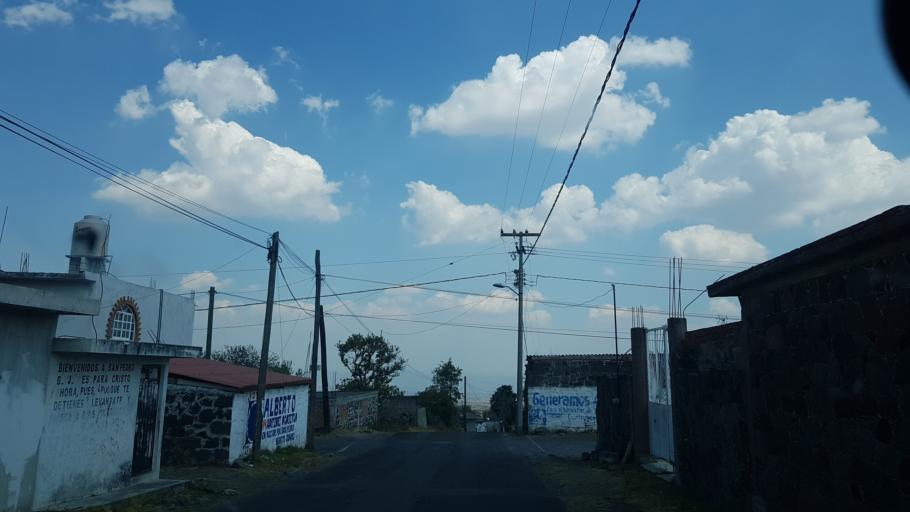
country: MX
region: Puebla
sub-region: Atlixco
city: San Pedro Benito Juarez
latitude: 18.9504
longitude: -98.5422
